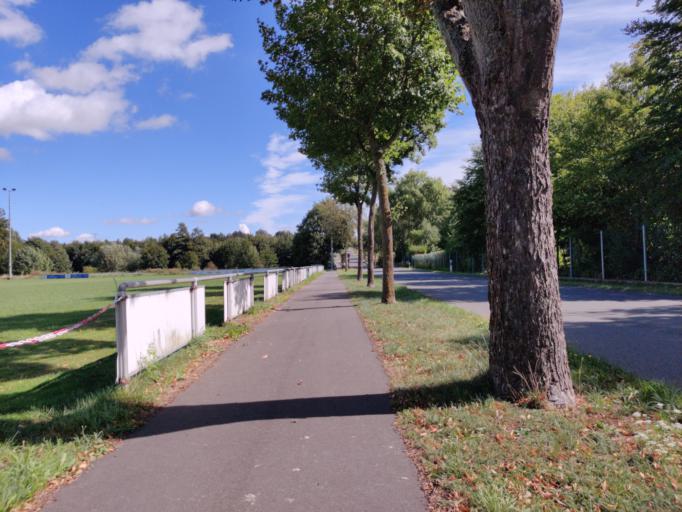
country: DE
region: Lower Saxony
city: Heere
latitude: 52.0684
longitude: 10.2557
